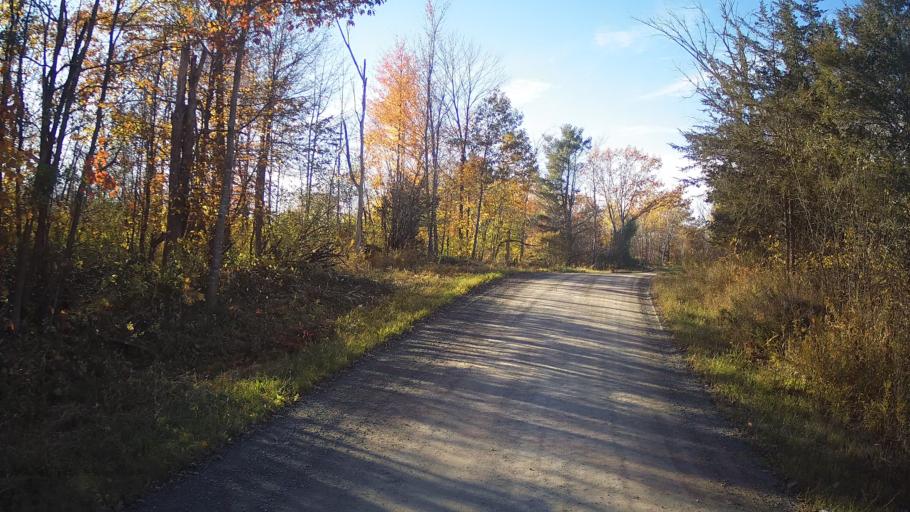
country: CA
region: Ontario
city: Perth
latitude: 44.7183
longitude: -76.4084
